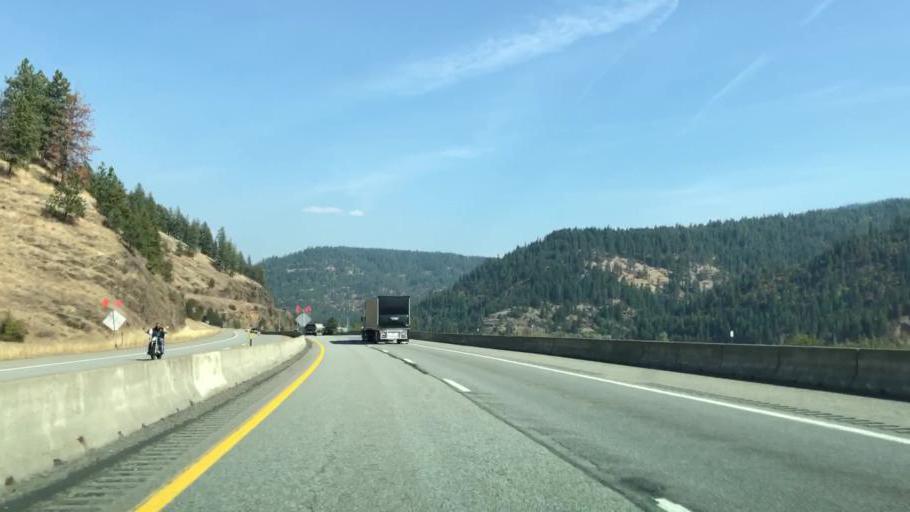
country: US
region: Idaho
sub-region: Kootenai County
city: Coeur d'Alene
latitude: 47.6237
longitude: -116.6620
